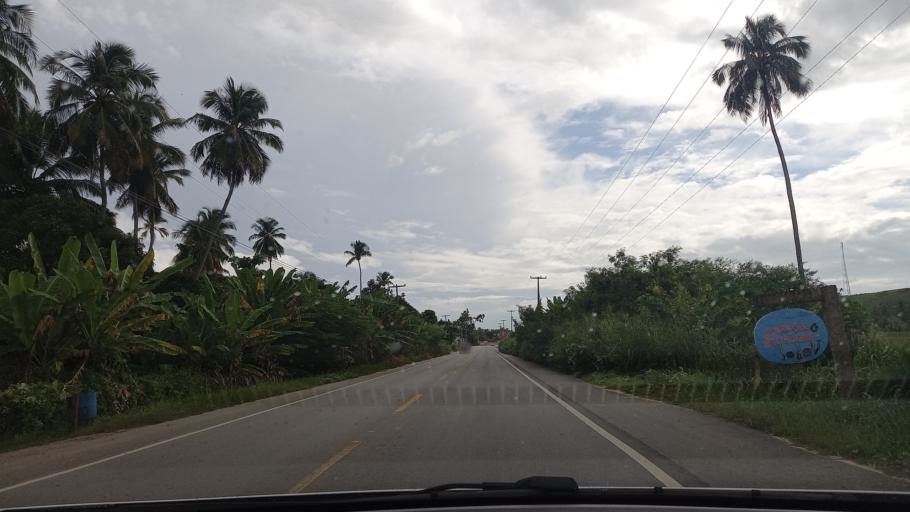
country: BR
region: Alagoas
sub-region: Maragogi
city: Maragogi
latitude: -8.9800
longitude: -35.1878
